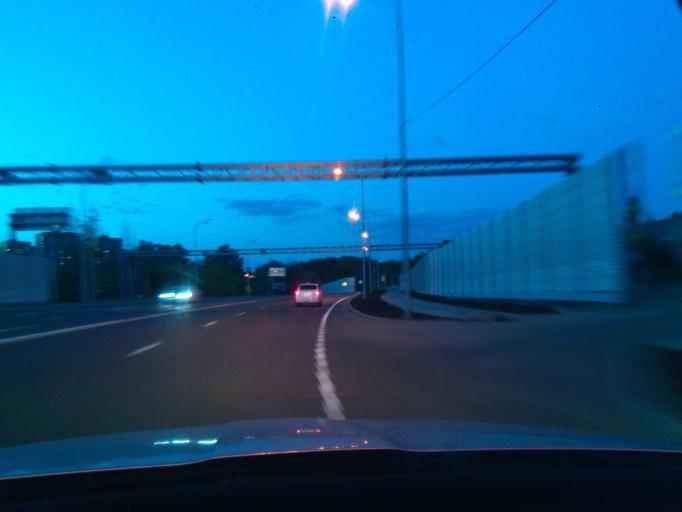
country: RU
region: Moskovskaya
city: Dolgoprudnyy
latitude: 55.9557
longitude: 37.5186
